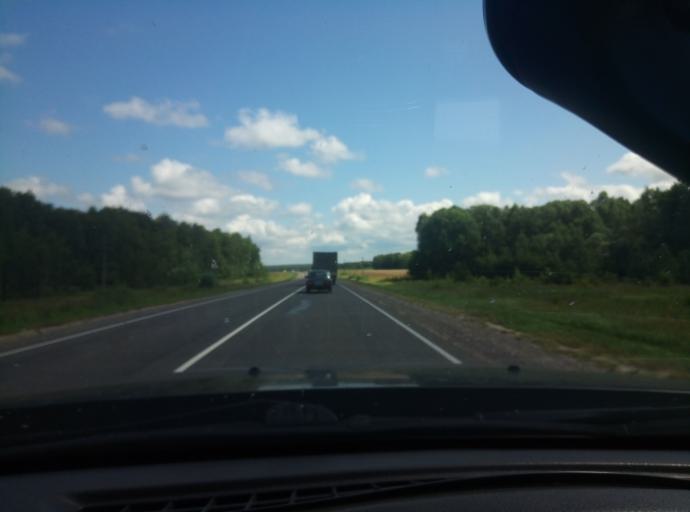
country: RU
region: Tula
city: Dubna
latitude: 54.3294
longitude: 36.9191
